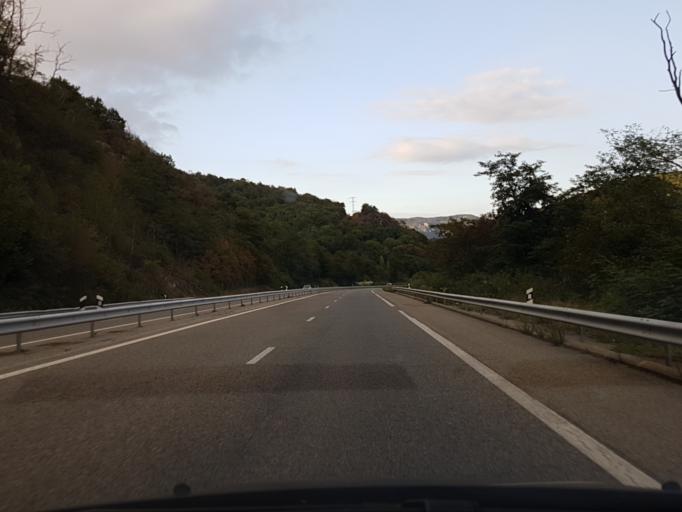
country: FR
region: Midi-Pyrenees
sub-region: Departement de l'Ariege
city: Mercus-Garrabet
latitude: 42.8974
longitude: 1.6318
